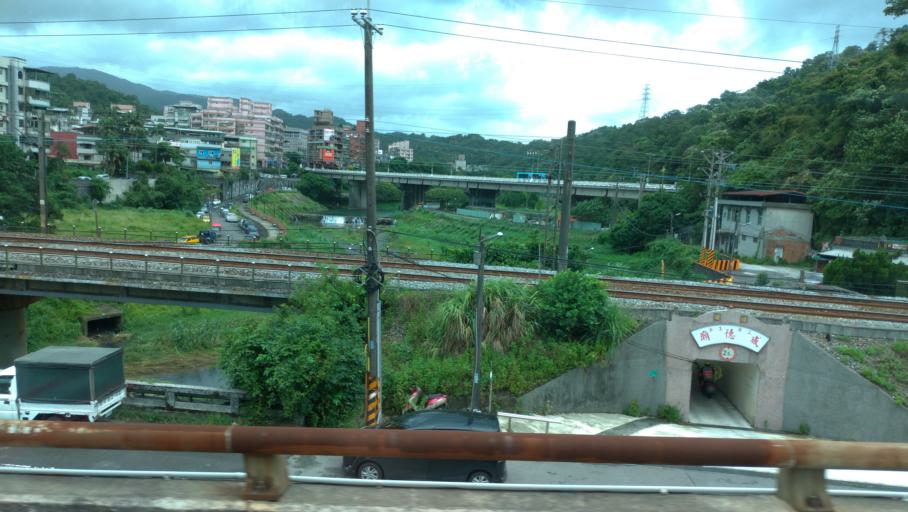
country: TW
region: Taiwan
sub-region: Keelung
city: Keelung
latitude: 25.1032
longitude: 121.7372
